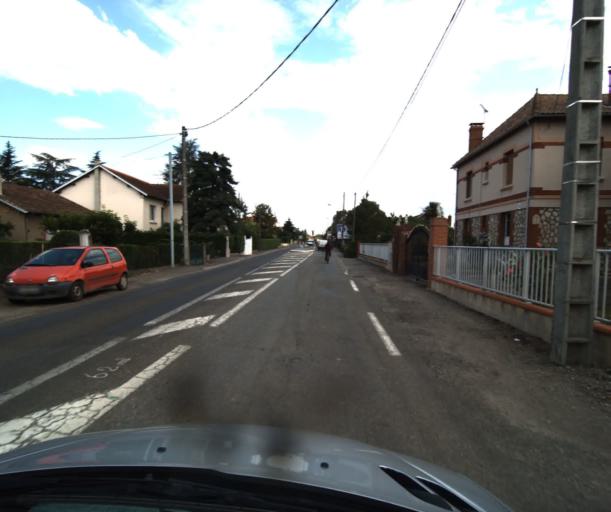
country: FR
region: Midi-Pyrenees
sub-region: Departement du Tarn-et-Garonne
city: Montauban
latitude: 44.0037
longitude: 1.3498
